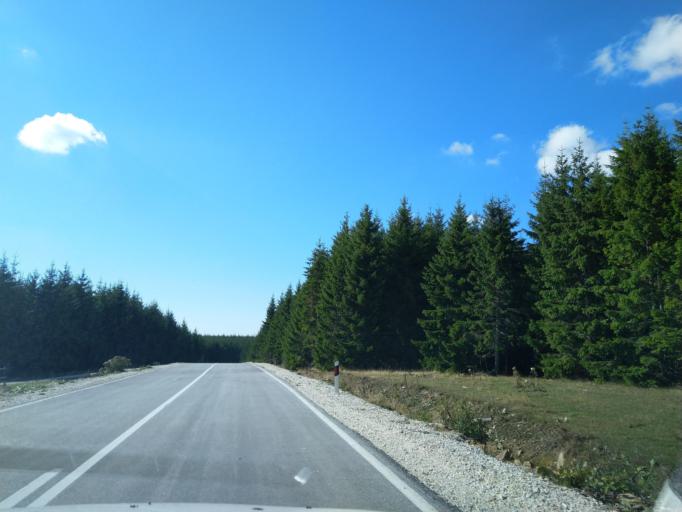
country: RS
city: Sokolovica
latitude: 43.2897
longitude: 20.3155
